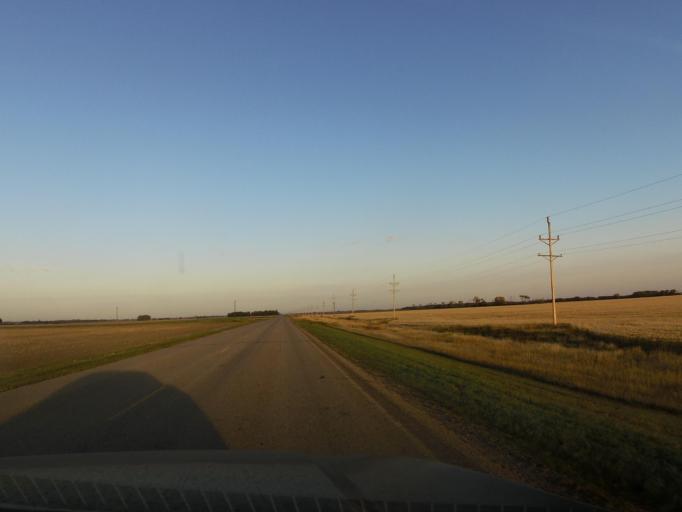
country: CA
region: Manitoba
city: Altona
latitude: 48.9633
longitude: -97.6108
